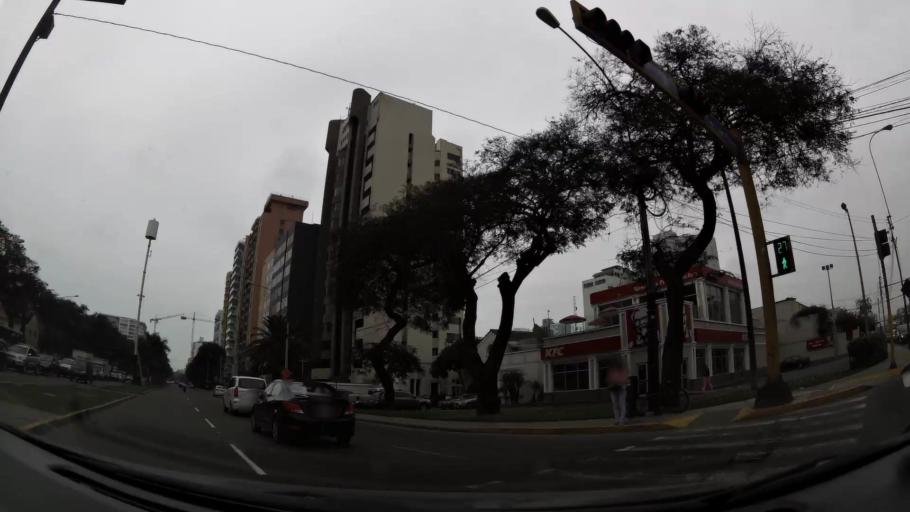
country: PE
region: Lima
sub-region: Lima
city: San Isidro
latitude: -12.0942
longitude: -77.0474
